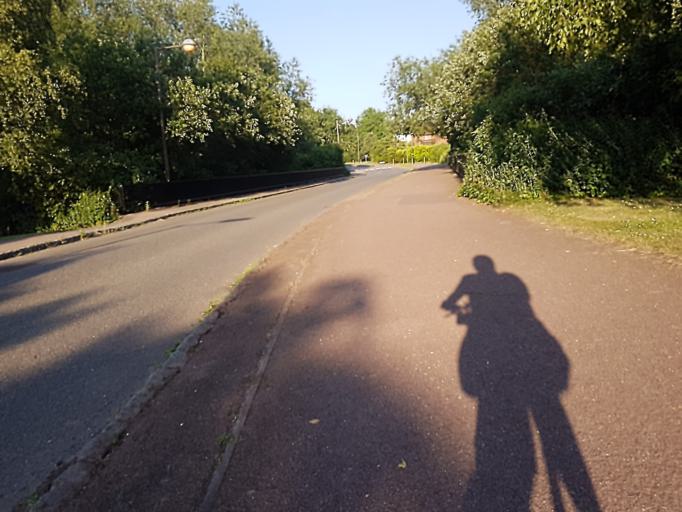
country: GB
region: England
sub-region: Milton Keynes
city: Loughton
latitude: 52.0342
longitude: -0.7850
